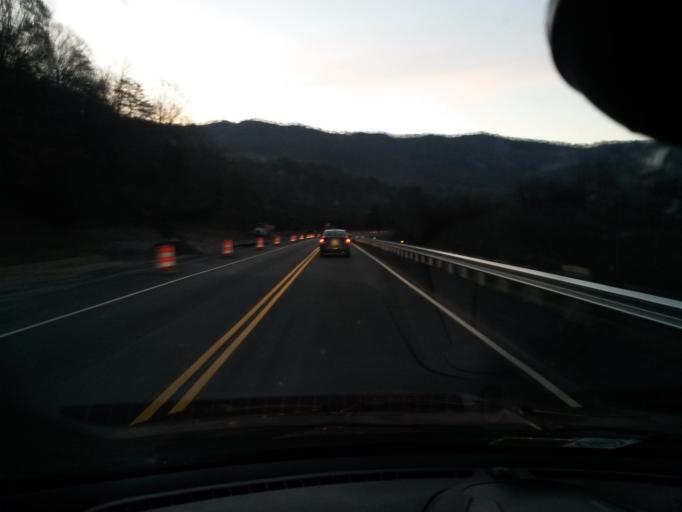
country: US
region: Virginia
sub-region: Alleghany County
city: Clifton Forge
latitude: 37.6732
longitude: -79.7973
